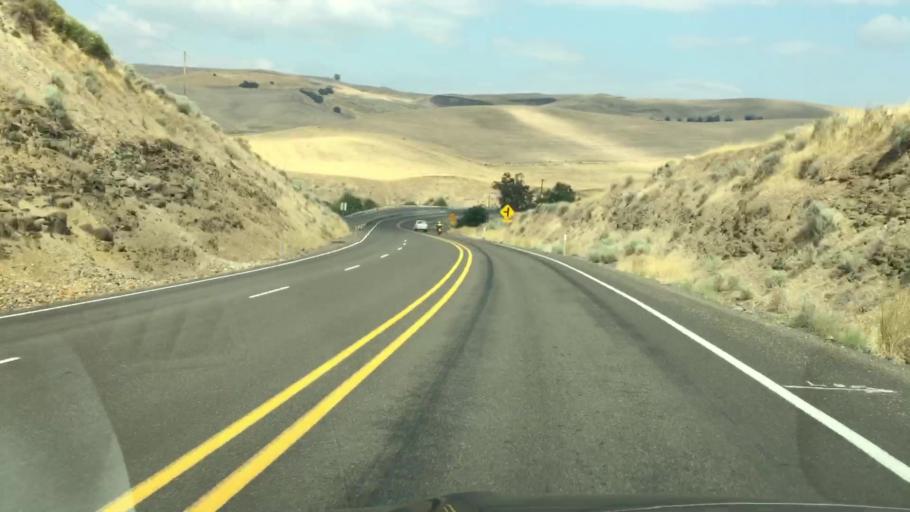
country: US
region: Oregon
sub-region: Wasco County
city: The Dalles
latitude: 45.5595
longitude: -121.1008
